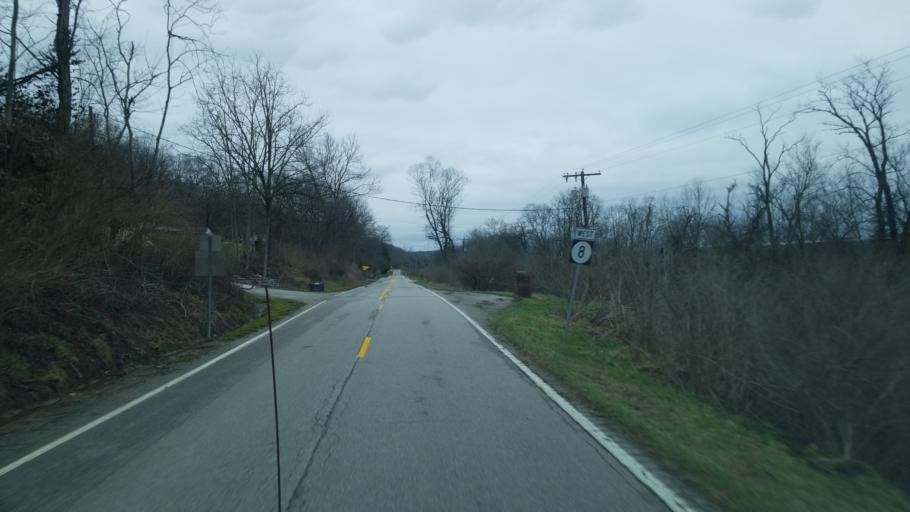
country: US
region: Ohio
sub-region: Clermont County
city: New Richmond
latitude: 38.9467
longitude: -84.2903
